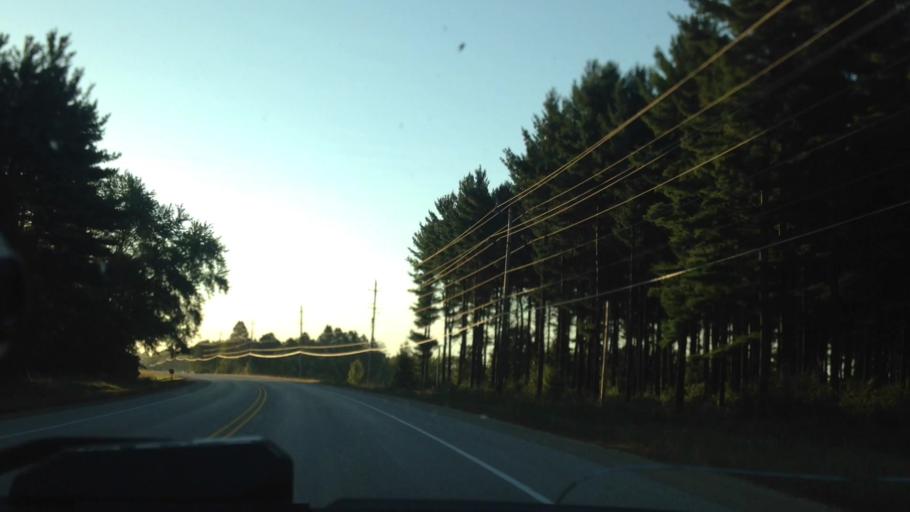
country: US
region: Wisconsin
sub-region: Washington County
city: Newburg
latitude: 43.4097
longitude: -88.0072
